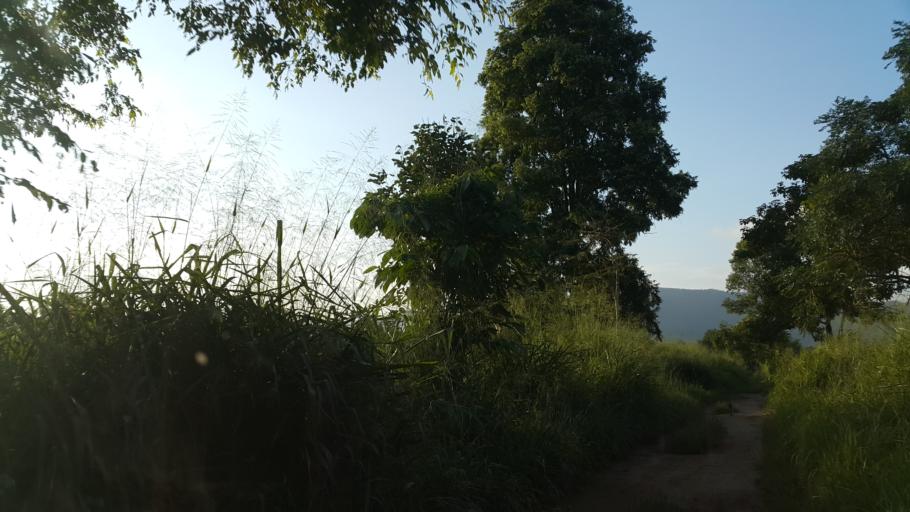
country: TH
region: Chiang Mai
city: Mae On
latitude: 18.7422
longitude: 99.2501
